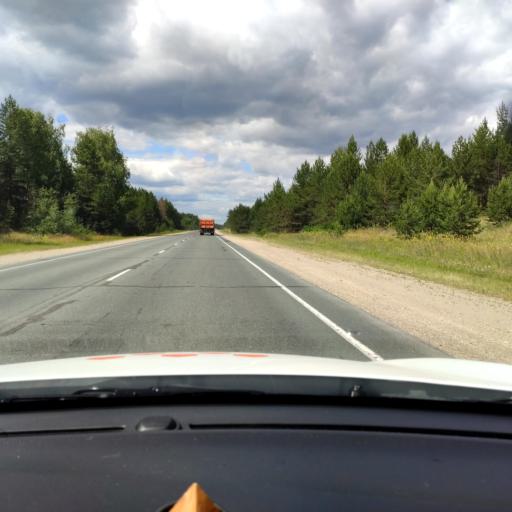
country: RU
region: Mariy-El
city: Krasnogorskiy
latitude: 56.0820
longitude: 48.3551
